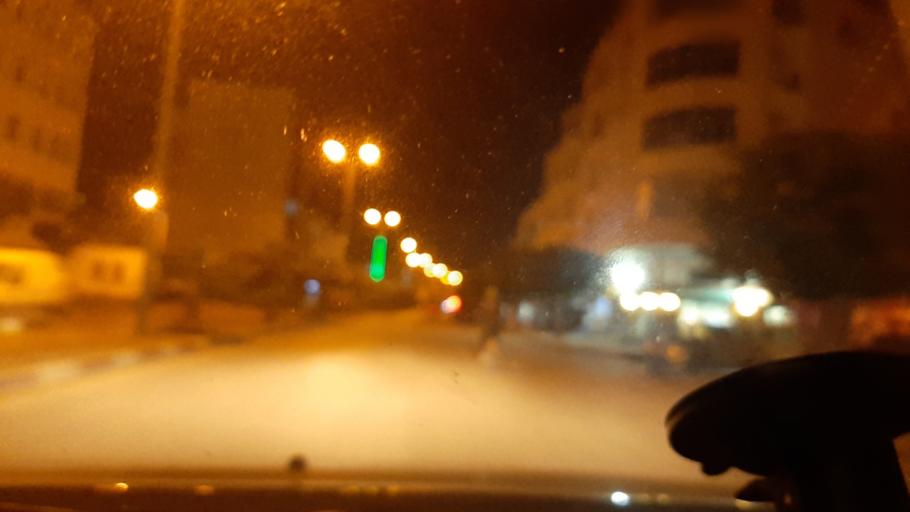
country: TN
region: Safaqis
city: Sfax
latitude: 34.7331
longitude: 10.7578
